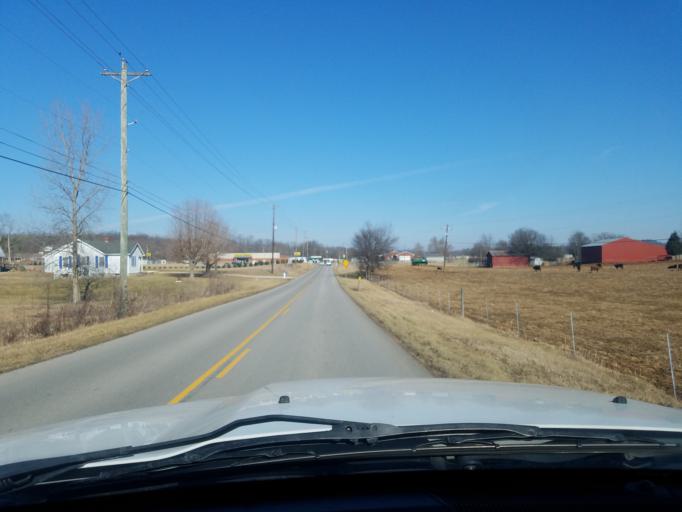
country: US
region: Kentucky
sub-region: Hardin County
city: Elizabethtown
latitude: 37.5740
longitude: -86.0370
